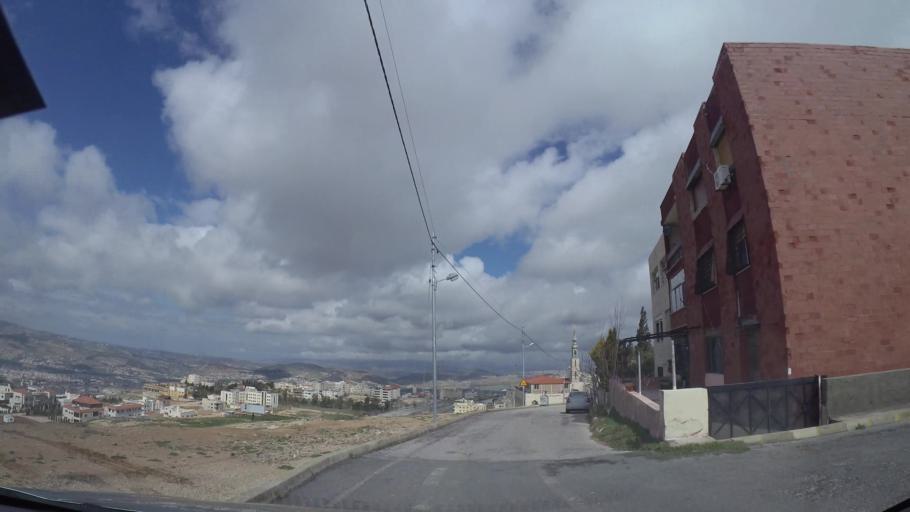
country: JO
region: Amman
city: Al Jubayhah
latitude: 32.0512
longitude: 35.8719
